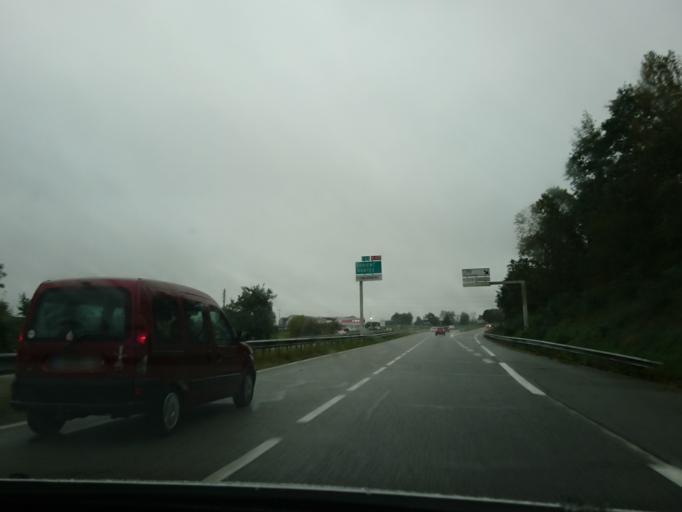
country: FR
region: Brittany
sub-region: Departement du Finistere
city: Ergue-Gaberic
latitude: 48.0029
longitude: -4.0561
